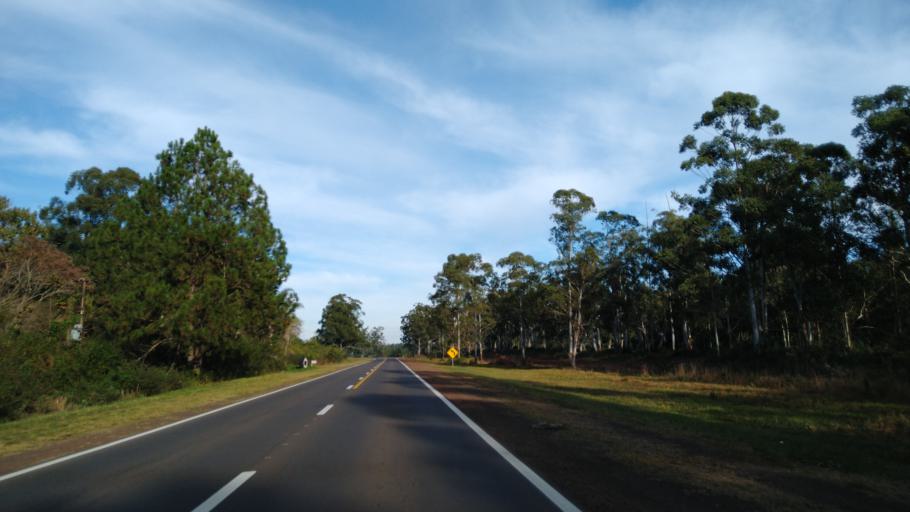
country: AR
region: Corrientes
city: Yapeyu
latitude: -29.4280
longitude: -56.8696
